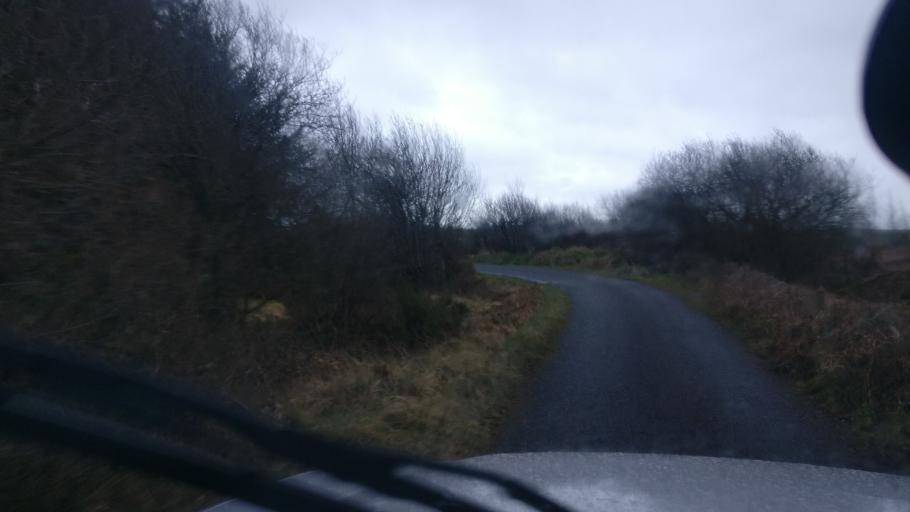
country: IE
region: Connaught
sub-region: County Galway
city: Loughrea
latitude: 53.2475
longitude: -8.4340
